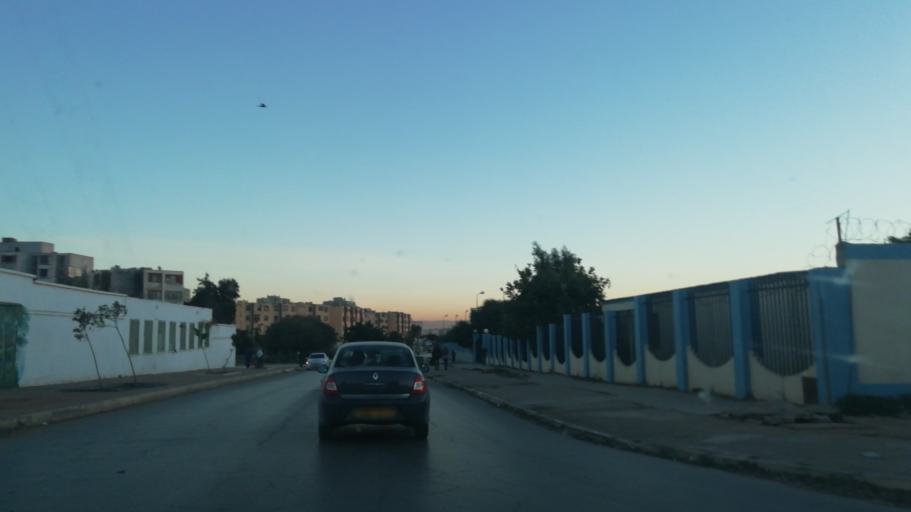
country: DZ
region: Oran
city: Bir el Djir
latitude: 35.7074
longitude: -0.5912
